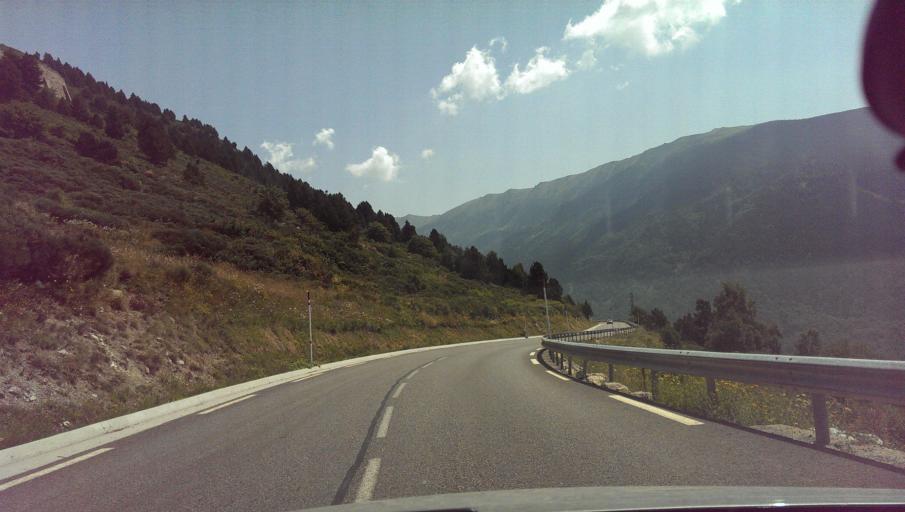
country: AD
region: Encamp
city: Pas de la Casa
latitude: 42.5530
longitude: 1.8209
